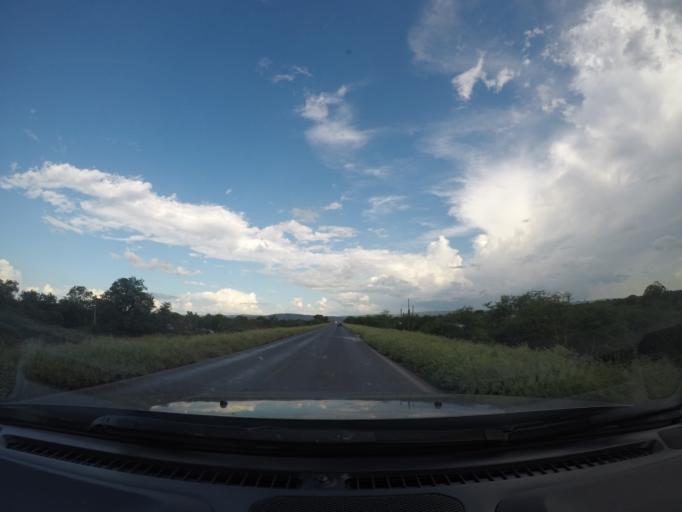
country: BR
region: Bahia
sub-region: Ibotirama
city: Ibotirama
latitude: -12.1758
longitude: -43.2506
